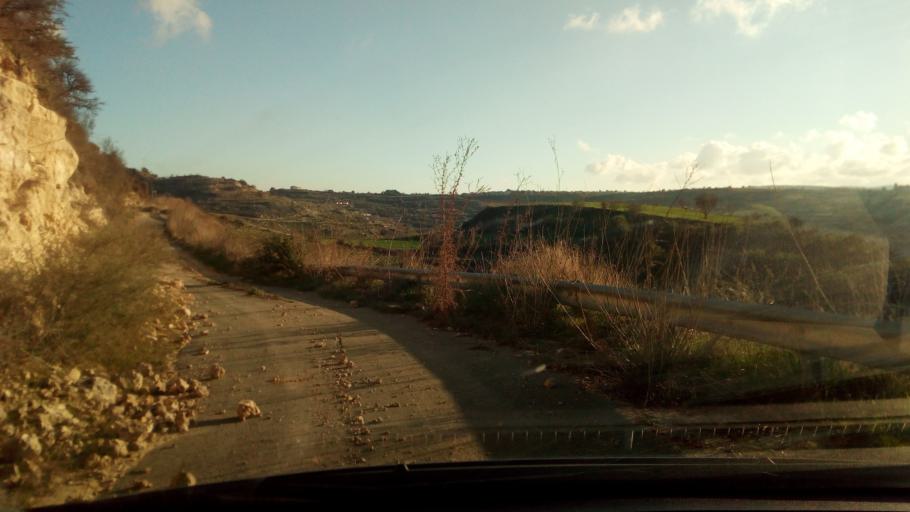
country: CY
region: Pafos
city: Tala
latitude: 34.9111
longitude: 32.5132
